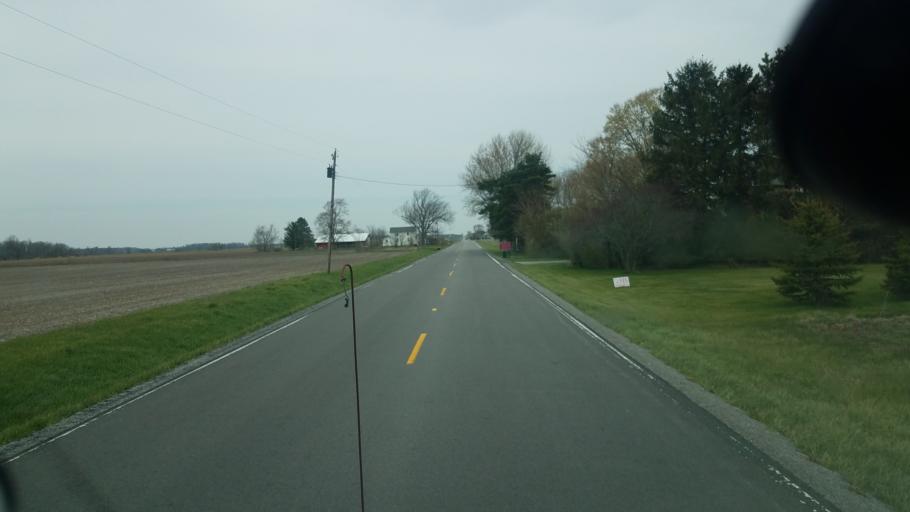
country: US
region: Ohio
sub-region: Wyandot County
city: Carey
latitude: 41.0120
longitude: -83.4776
